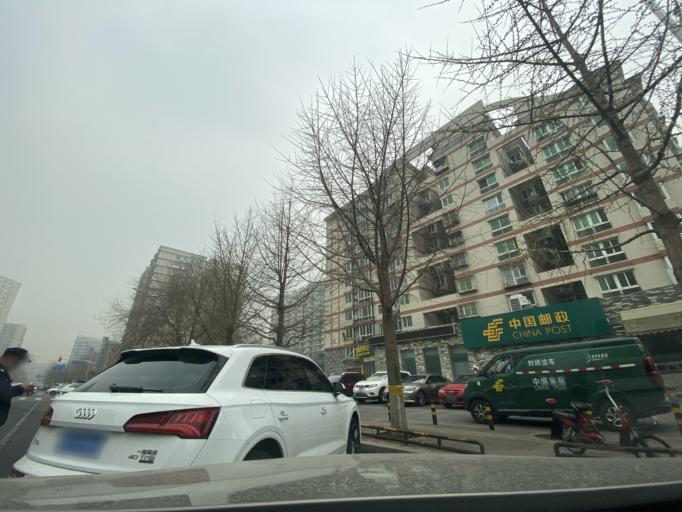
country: CN
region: Beijing
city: Sijiqing
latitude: 39.9607
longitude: 116.2741
